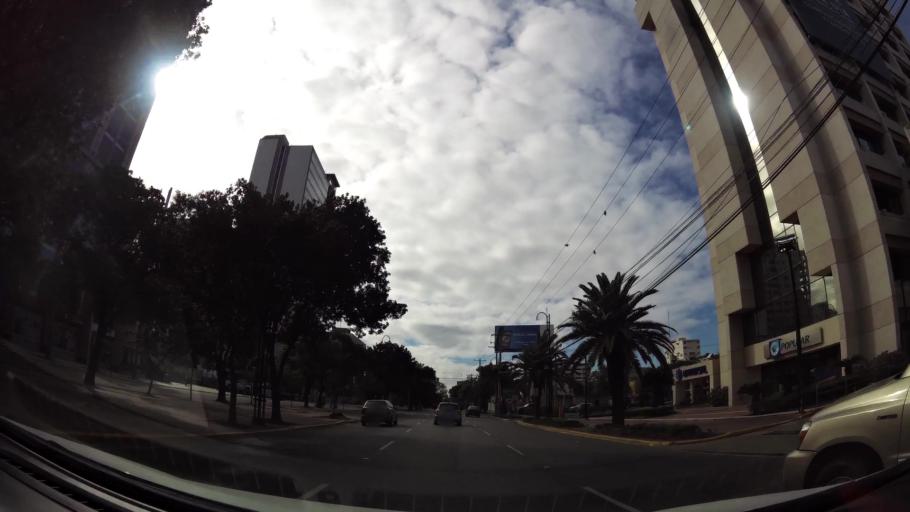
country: DO
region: Nacional
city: La Julia
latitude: 18.4695
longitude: -69.9401
